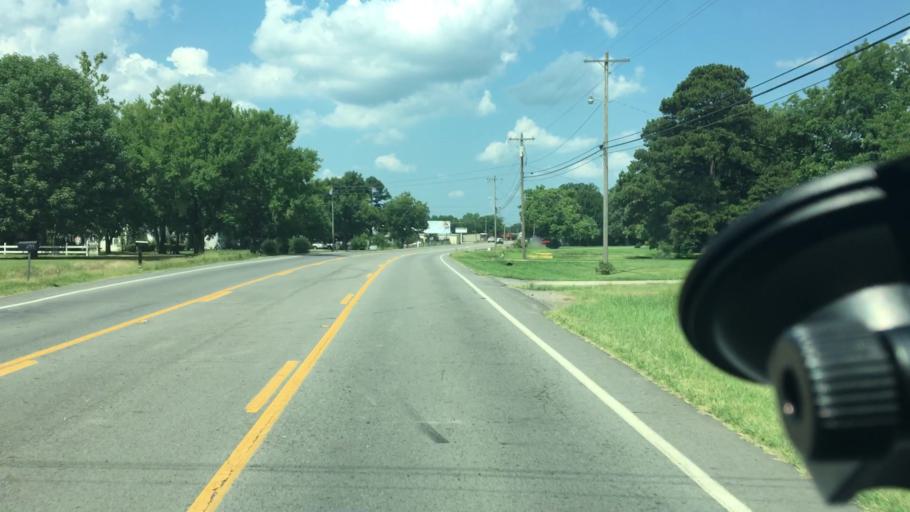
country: US
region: Arkansas
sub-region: Logan County
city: Paris
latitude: 35.2921
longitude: -93.7065
